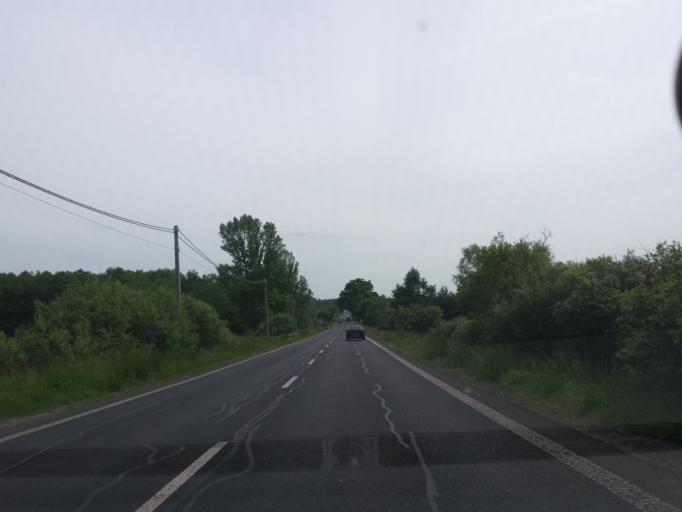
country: CZ
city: Novy Bor
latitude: 50.7275
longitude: 14.5462
